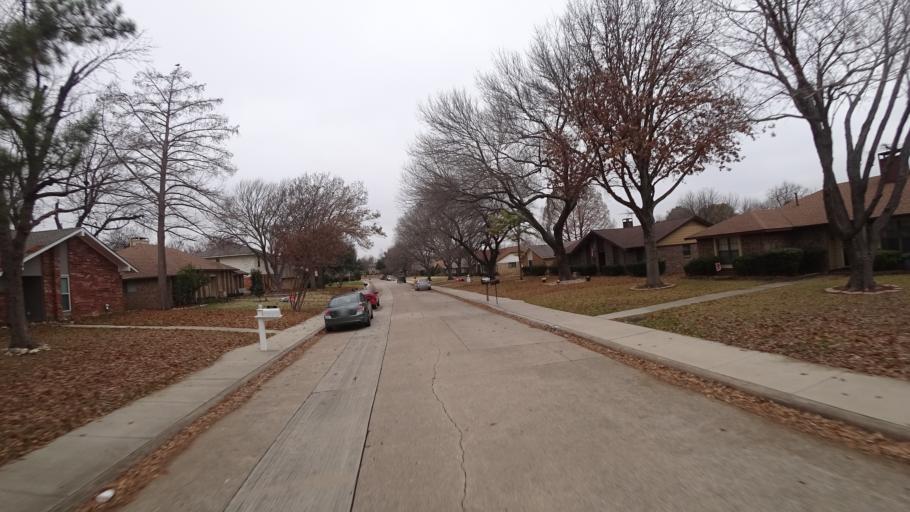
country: US
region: Texas
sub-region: Denton County
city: Highland Village
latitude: 33.0520
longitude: -97.0417
